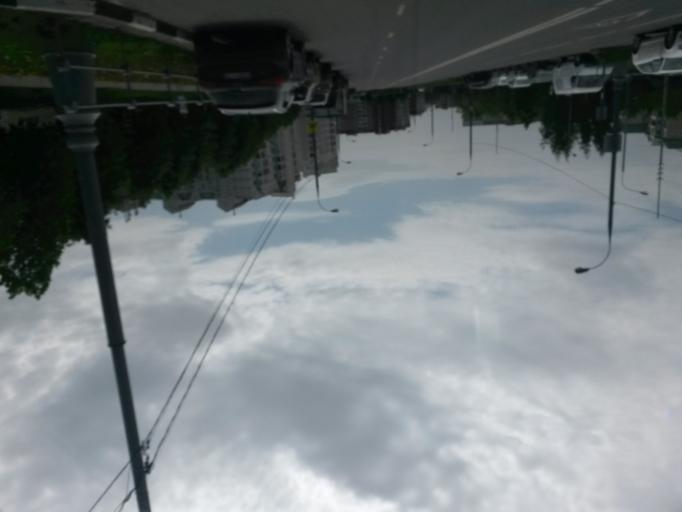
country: RU
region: Moskovskaya
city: Shcherbinka
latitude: 55.5411
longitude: 37.5331
